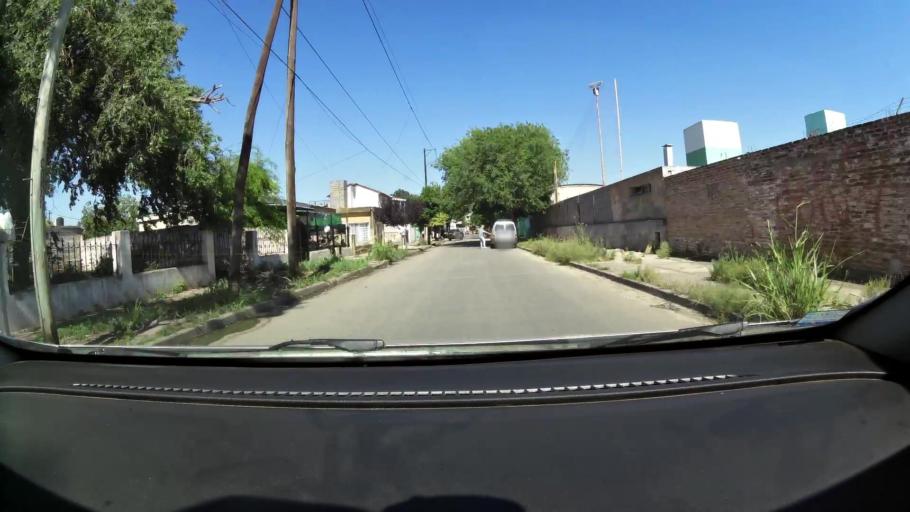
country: AR
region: Cordoba
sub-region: Departamento de Capital
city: Cordoba
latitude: -31.4399
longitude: -64.1405
